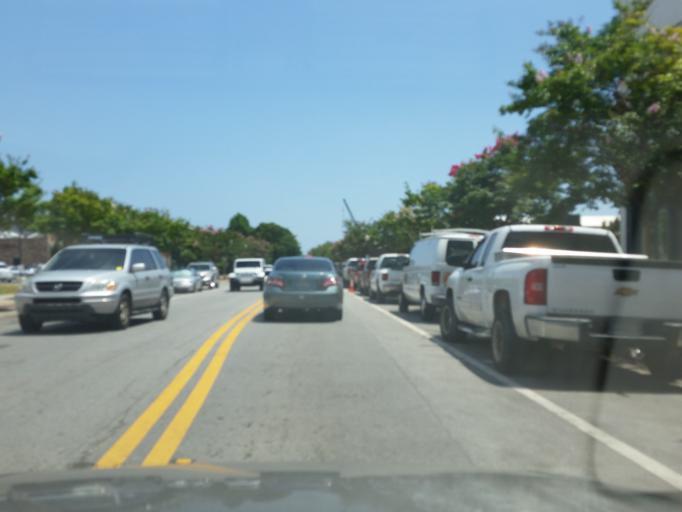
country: US
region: Florida
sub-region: Escambia County
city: Pensacola
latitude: 30.4073
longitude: -87.2141
